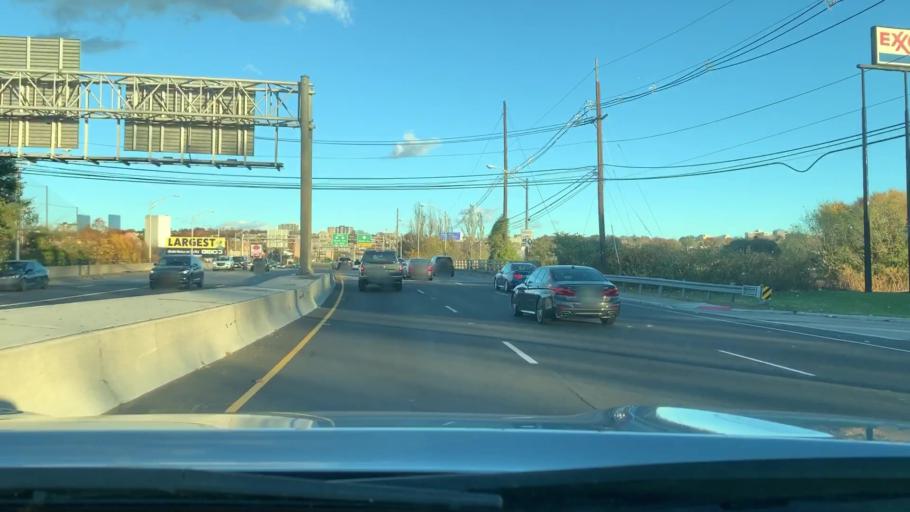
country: US
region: New Jersey
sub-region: Bergen County
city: Ridgefield
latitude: 40.8445
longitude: -74.0126
